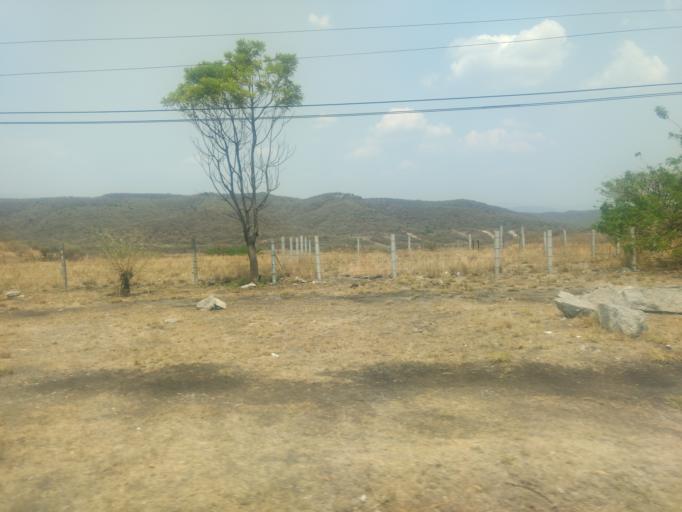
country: MX
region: Morelos
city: Ahuehuetzingo
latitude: 18.6575
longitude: -99.2965
